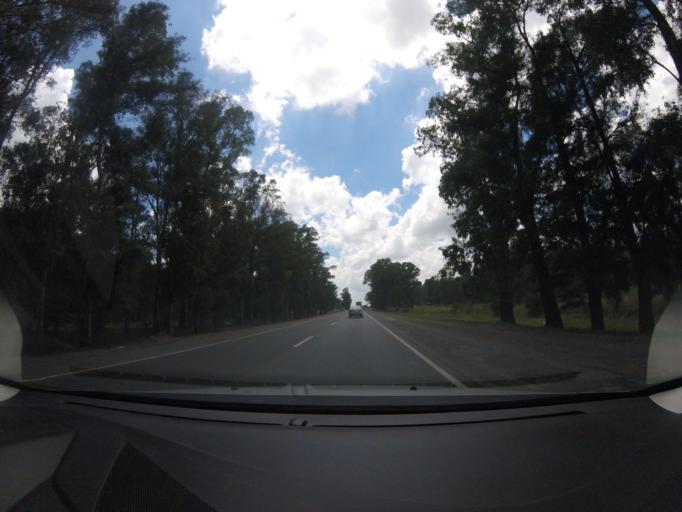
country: AR
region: Buenos Aires
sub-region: Partido de Las Flores
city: Las Flores
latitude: -36.0455
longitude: -59.0850
